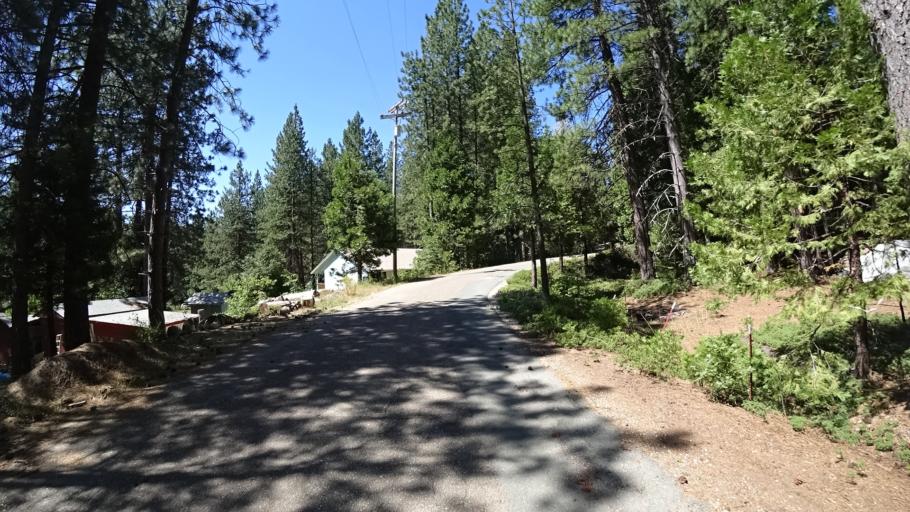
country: US
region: California
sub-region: Amador County
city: Pioneer
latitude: 38.4448
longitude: -120.4293
